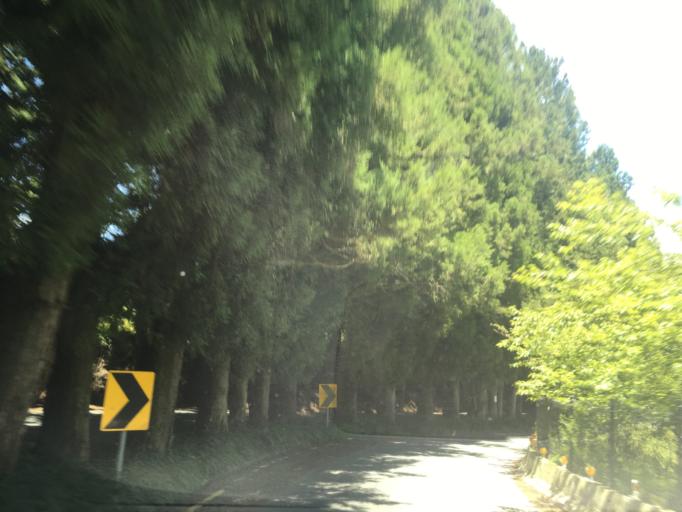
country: TW
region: Taiwan
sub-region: Nantou
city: Puli
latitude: 24.2493
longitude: 121.2481
